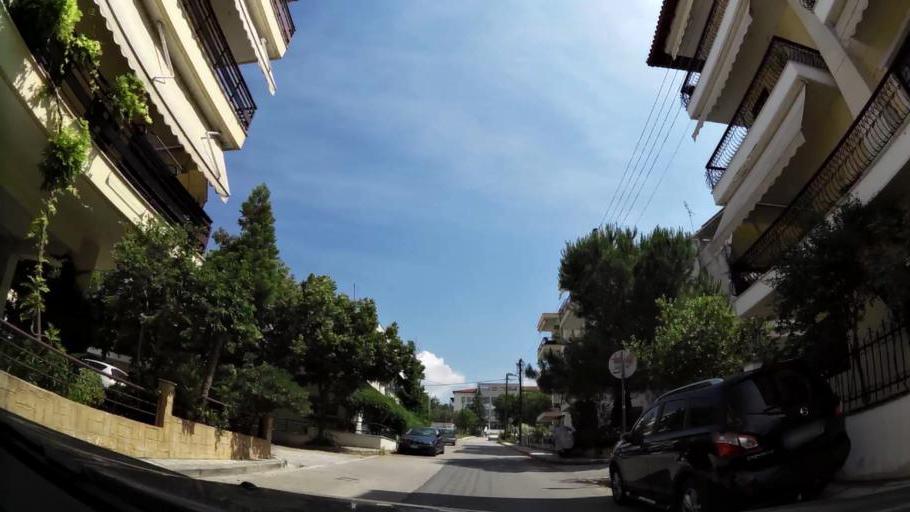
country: GR
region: Central Macedonia
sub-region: Nomos Thessalonikis
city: Triandria
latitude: 40.6156
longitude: 22.9815
